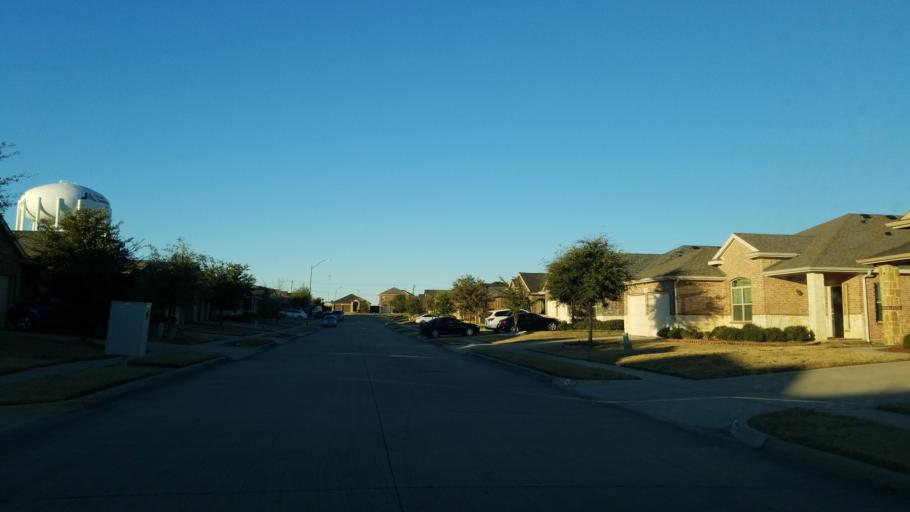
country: US
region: Texas
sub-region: Tarrant County
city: Arlington
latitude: 32.7328
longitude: -97.0530
